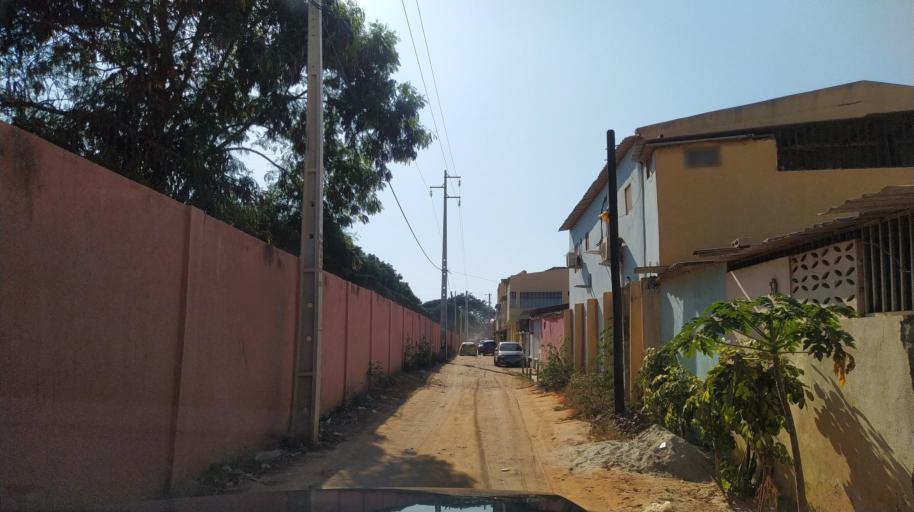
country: AO
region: Luanda
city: Luanda
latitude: -8.9052
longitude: 13.1831
